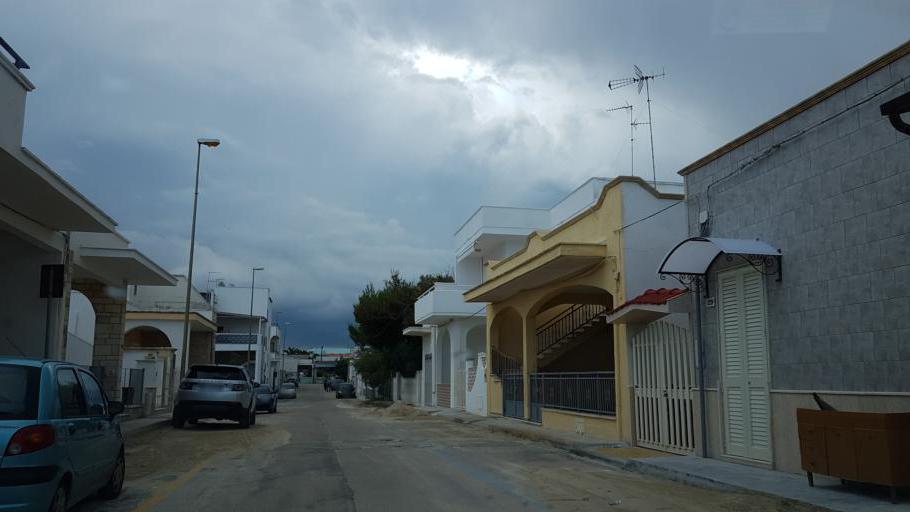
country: IT
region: Apulia
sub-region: Provincia di Lecce
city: Porto Cesareo
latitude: 40.2866
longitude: 17.8548
